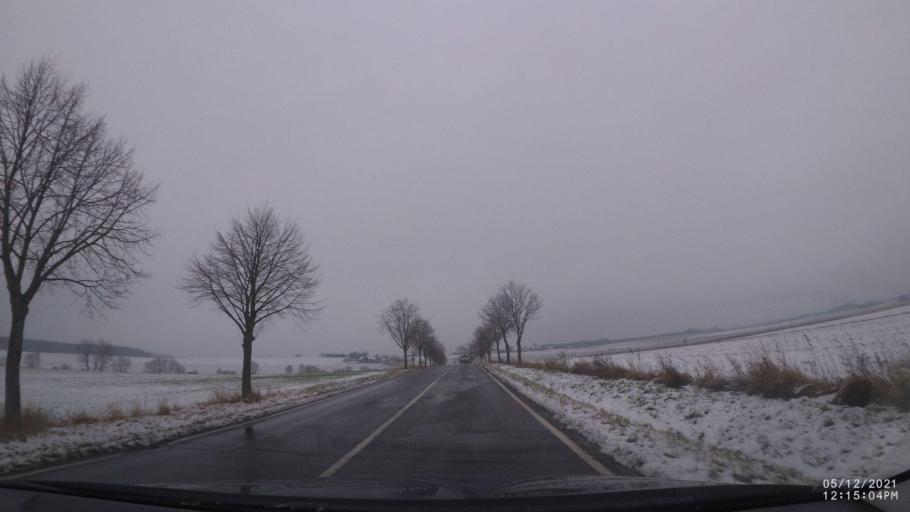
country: CZ
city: Ceske Mezirici
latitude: 50.3052
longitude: 16.0405
